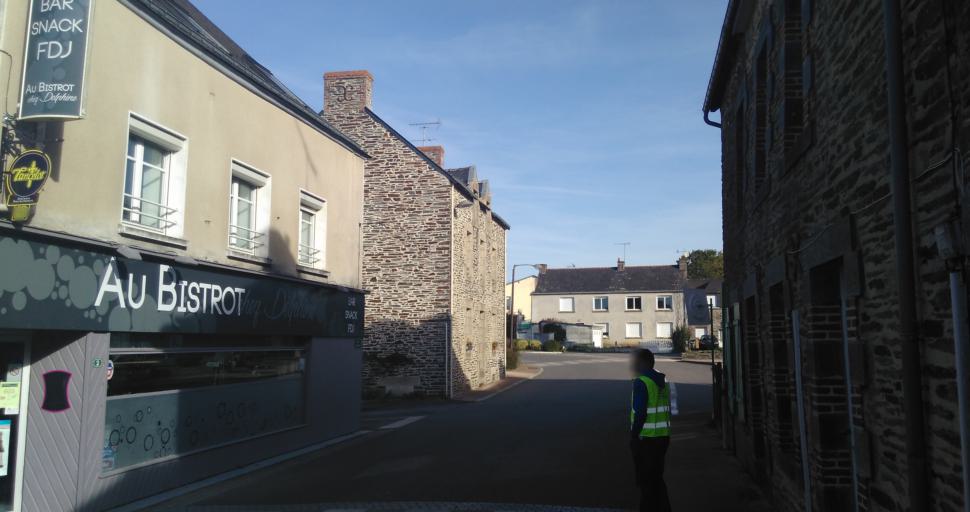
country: FR
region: Brittany
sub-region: Departement du Morbihan
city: Peillac
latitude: 47.7398
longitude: -2.2129
